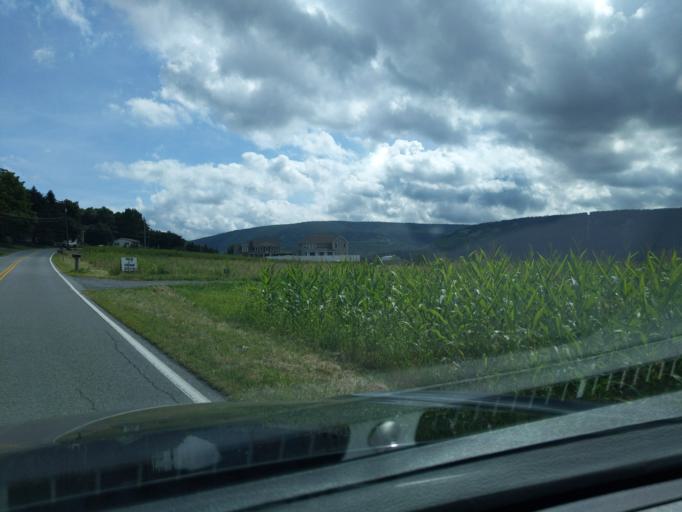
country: US
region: Pennsylvania
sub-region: Blair County
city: Duncansville
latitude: 40.3948
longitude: -78.4293
